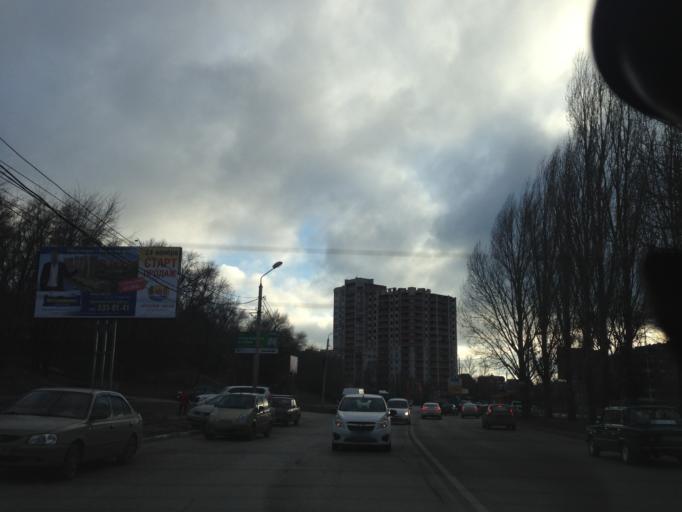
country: RU
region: Rostov
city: Temernik
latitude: 47.2927
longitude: 39.7347
